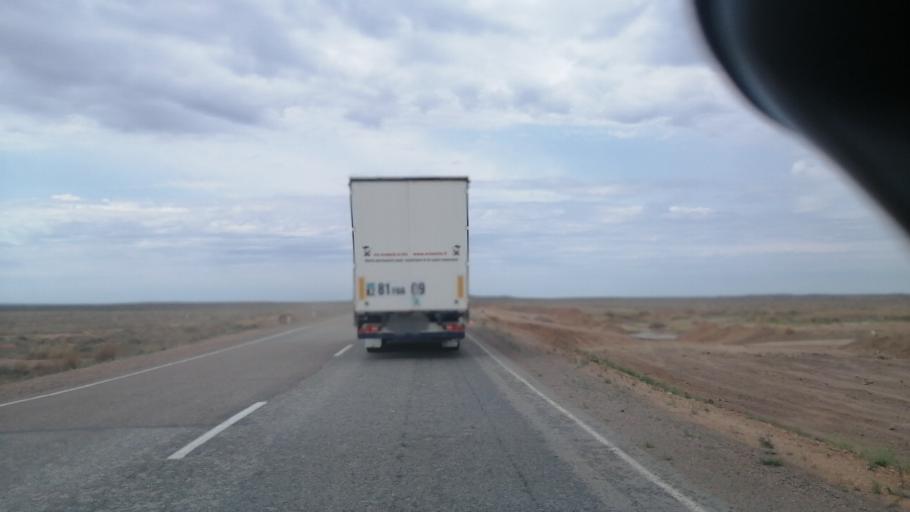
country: KZ
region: Qaraghandy
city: Saryshaghan
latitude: 46.4103
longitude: 73.8990
